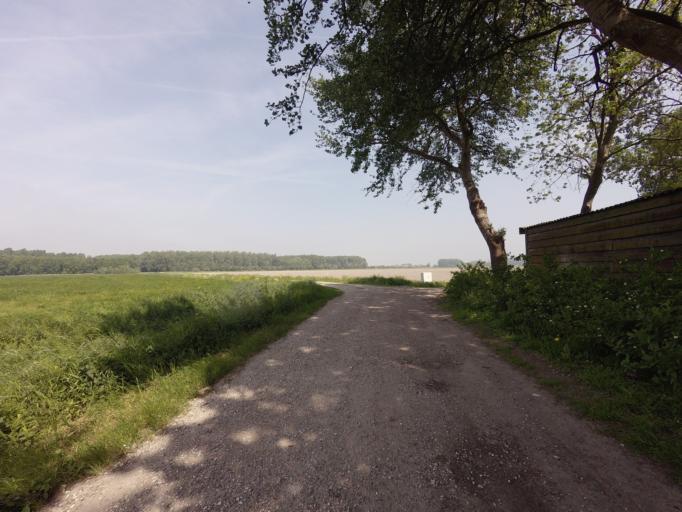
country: NL
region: South Holland
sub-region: Gemeente Hellevoetsluis
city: Hellevoetsluis
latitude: 51.8255
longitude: 4.1751
